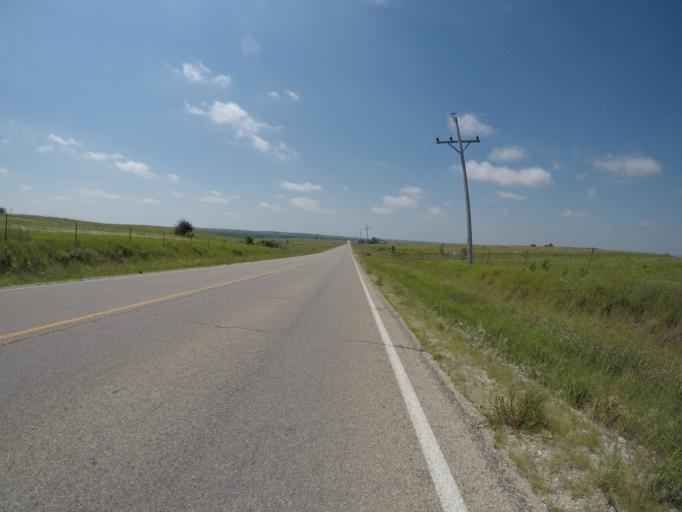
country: US
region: Kansas
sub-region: Pottawatomie County
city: Westmoreland
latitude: 39.3850
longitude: -96.4267
